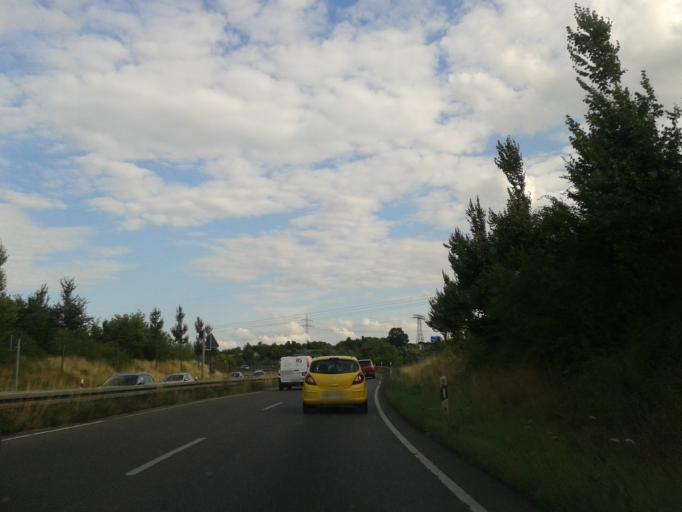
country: DE
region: Saxony
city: Bannewitz
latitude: 51.0126
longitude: 13.7234
